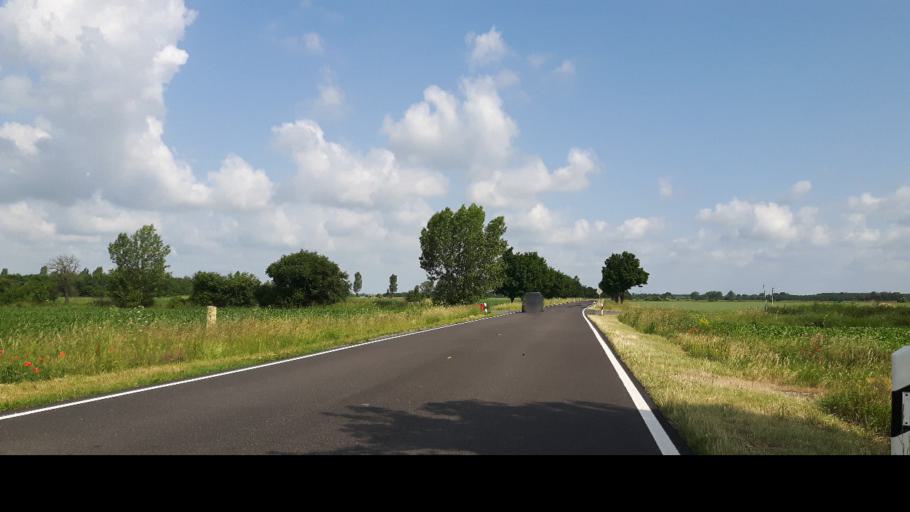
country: DE
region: Saxony
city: Rackwitz
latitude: 51.4440
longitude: 12.3482
